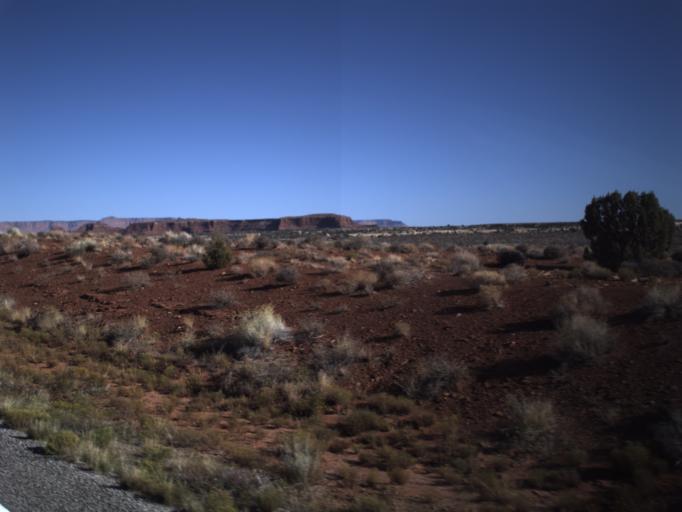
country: US
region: Utah
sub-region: San Juan County
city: Blanding
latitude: 37.7780
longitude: -110.2904
